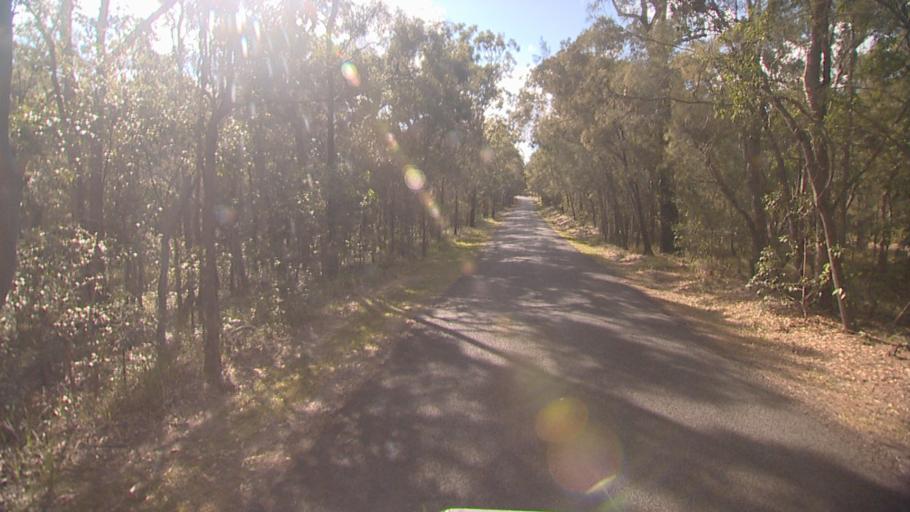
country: AU
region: Queensland
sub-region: Logan
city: Beenleigh
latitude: -27.6543
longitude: 153.2298
